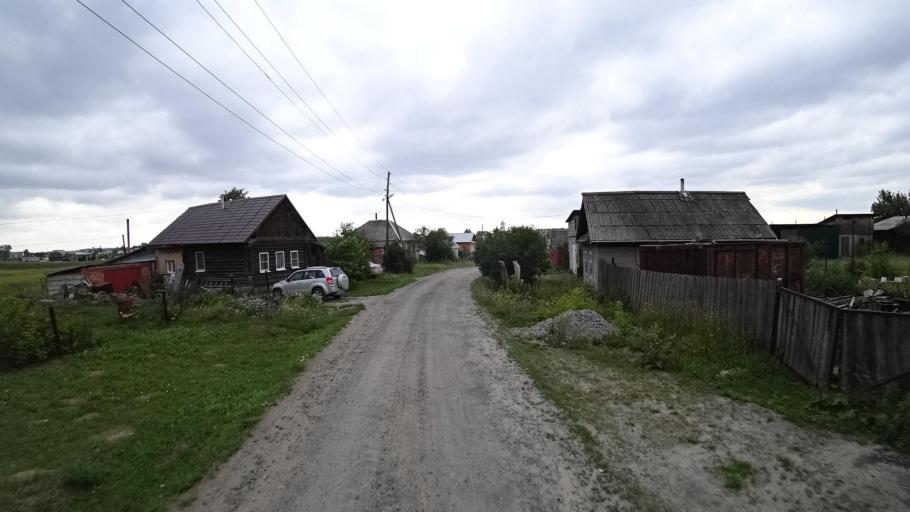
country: RU
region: Sverdlovsk
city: Kamyshlov
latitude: 56.8516
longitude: 62.6781
